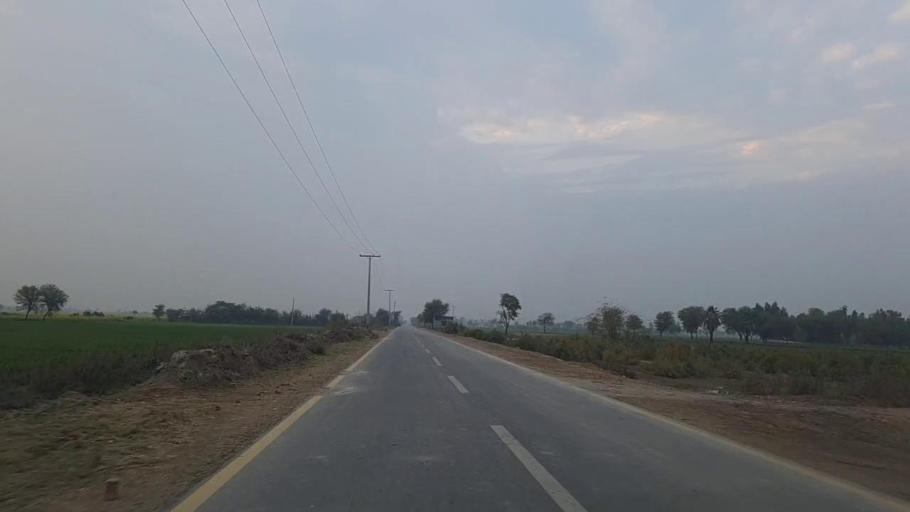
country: PK
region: Sindh
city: Jam Sahib
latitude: 26.3144
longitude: 68.5762
